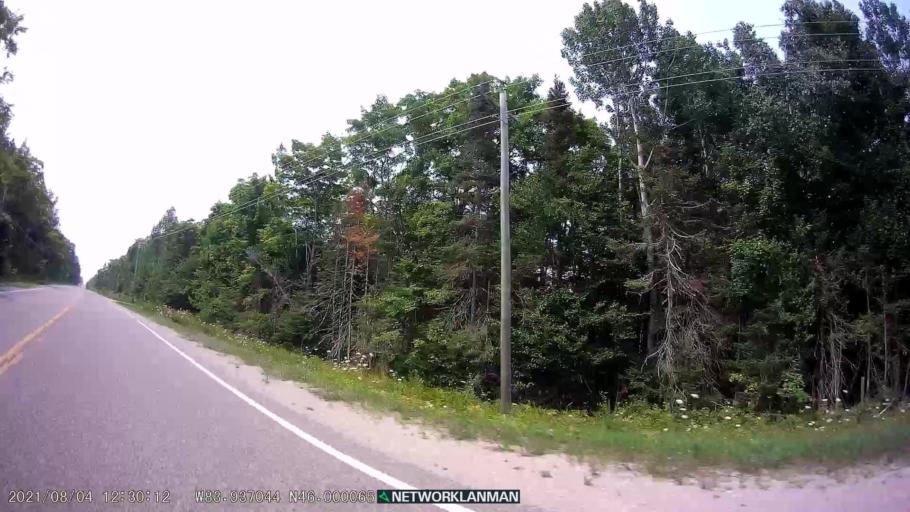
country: CA
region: Ontario
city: Thessalon
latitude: 46.0001
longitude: -83.9377
